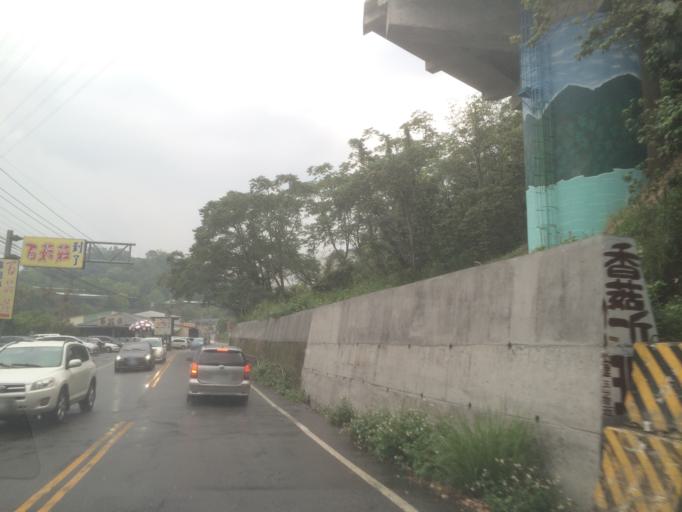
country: TW
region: Taiwan
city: Fengyuan
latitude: 24.1816
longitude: 120.8158
